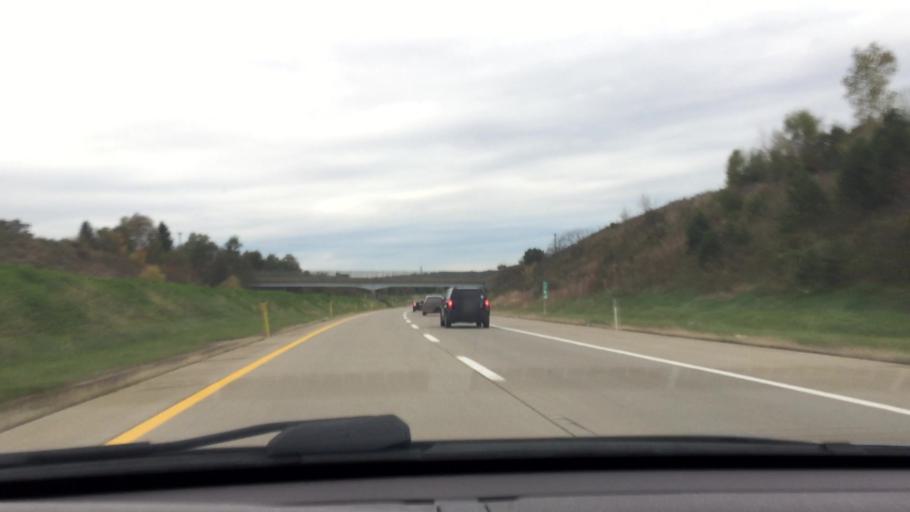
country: US
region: Pennsylvania
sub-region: Lawrence County
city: Oakland
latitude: 40.9680
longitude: -80.4000
